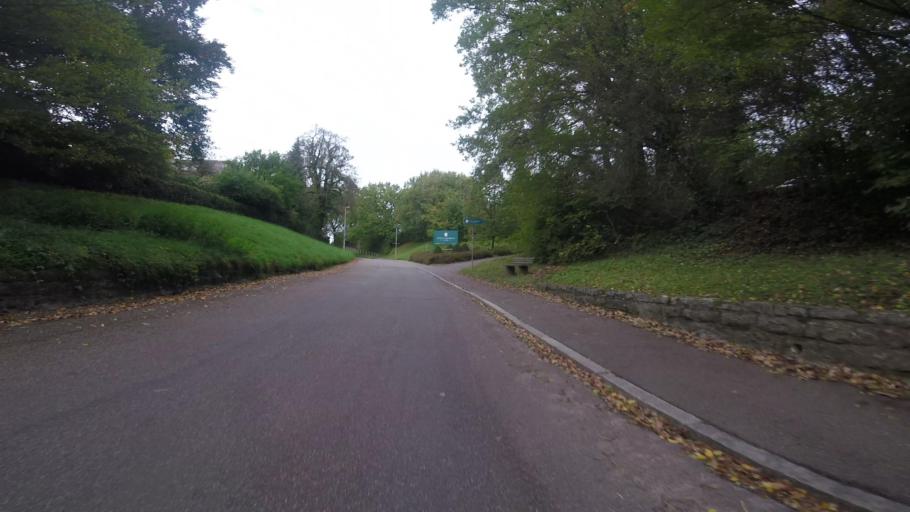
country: DE
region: Baden-Wuerttemberg
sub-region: Regierungsbezirk Stuttgart
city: Backnang
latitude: 48.9504
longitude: 9.4265
